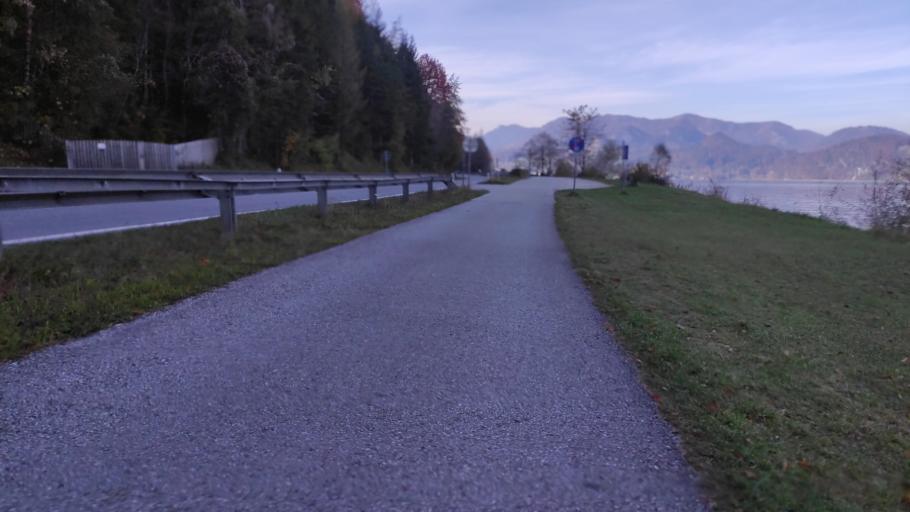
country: AT
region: Salzburg
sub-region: Politischer Bezirk Salzburg-Umgebung
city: Sankt Gilgen
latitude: 47.7400
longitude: 13.3922
